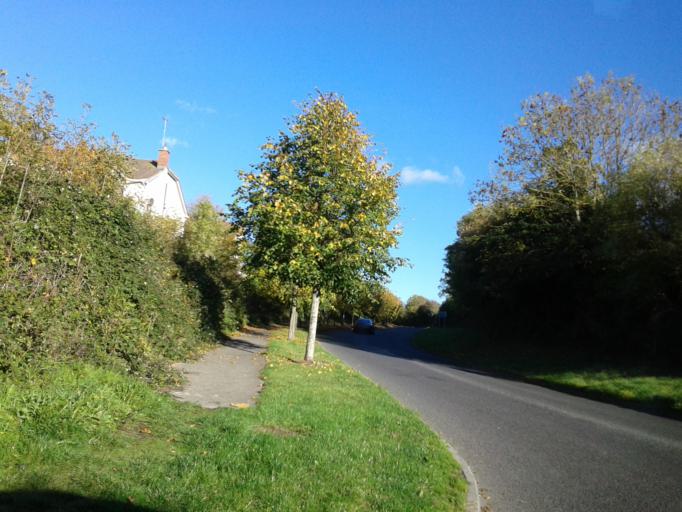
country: IE
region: Leinster
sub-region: Lu
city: Tullyallen
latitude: 53.7148
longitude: -6.3891
